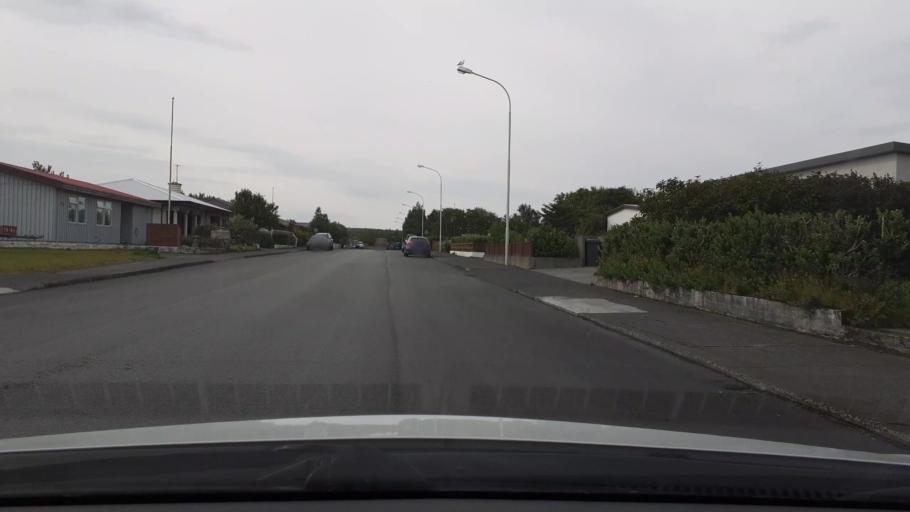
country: IS
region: Southern Peninsula
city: Reykjanesbaer
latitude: 63.9870
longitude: -22.5525
